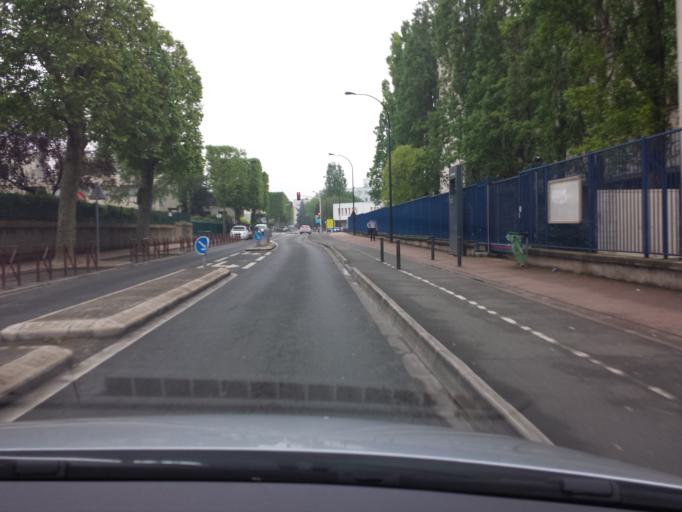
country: FR
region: Ile-de-France
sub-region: Departement du Val-de-Marne
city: L'Hay-les-Roses
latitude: 48.7884
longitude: 2.3241
